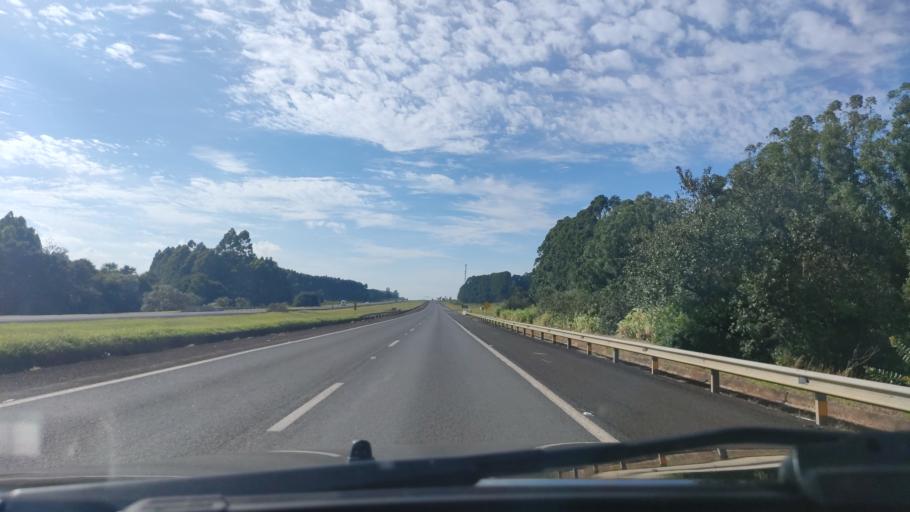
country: BR
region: Sao Paulo
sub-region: Itatinga
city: Itatinga
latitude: -22.9961
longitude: -48.7439
